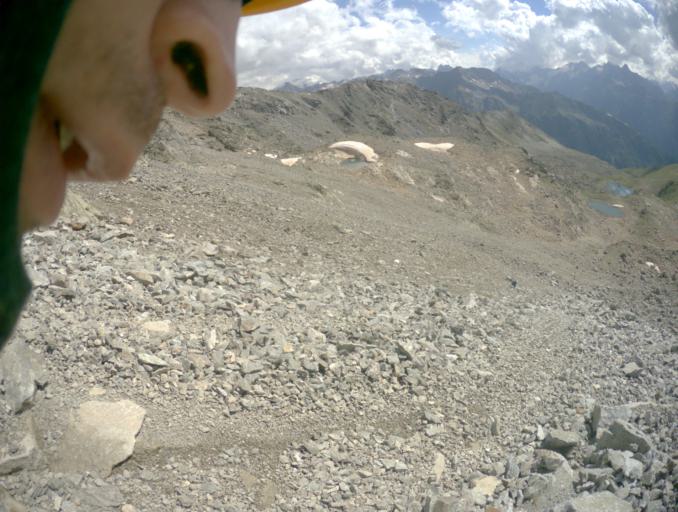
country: RU
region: Karachayevo-Cherkesiya
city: Uchkulan
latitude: 43.3182
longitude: 42.0770
